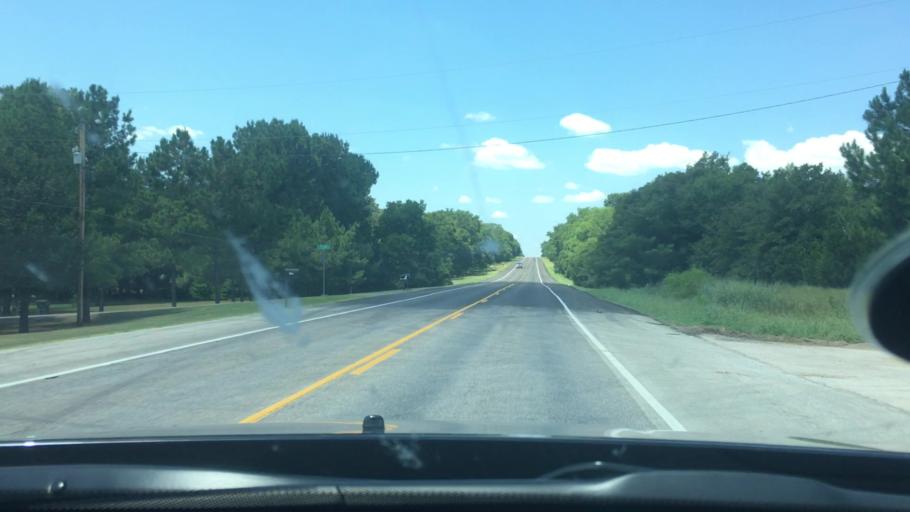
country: US
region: Oklahoma
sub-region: Carter County
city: Dickson
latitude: 34.1873
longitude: -96.9437
